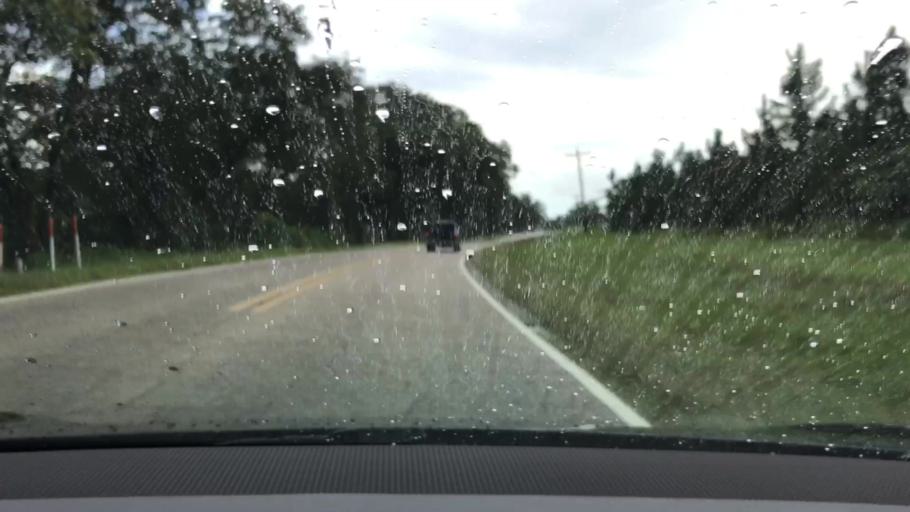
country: US
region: Alabama
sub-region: Geneva County
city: Samson
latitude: 31.1259
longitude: -86.1267
